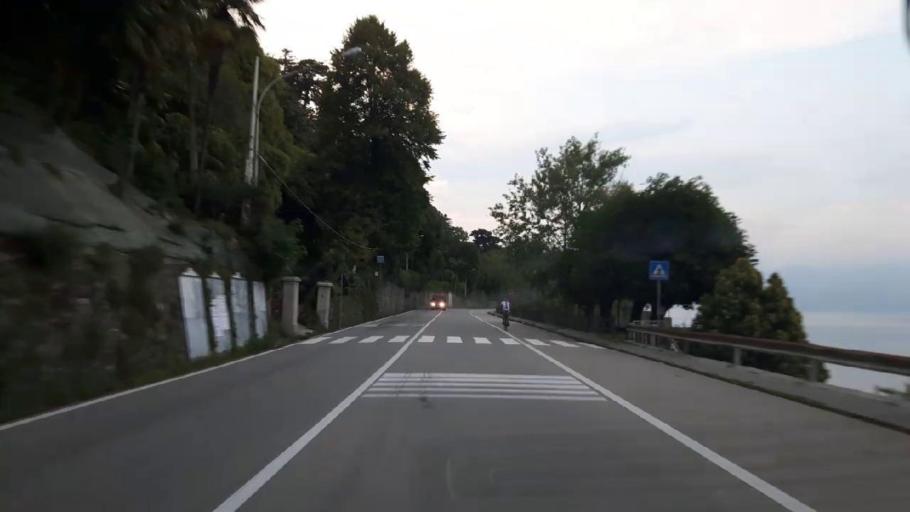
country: IT
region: Piedmont
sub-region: Provincia Verbano-Cusio-Ossola
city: Belgirate
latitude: 45.8432
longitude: 8.5731
